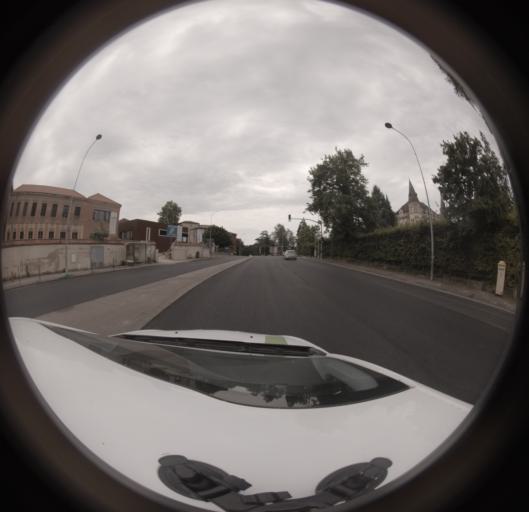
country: FR
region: Midi-Pyrenees
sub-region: Departement du Tarn-et-Garonne
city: Montauban
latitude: 44.0092
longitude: 1.3595
